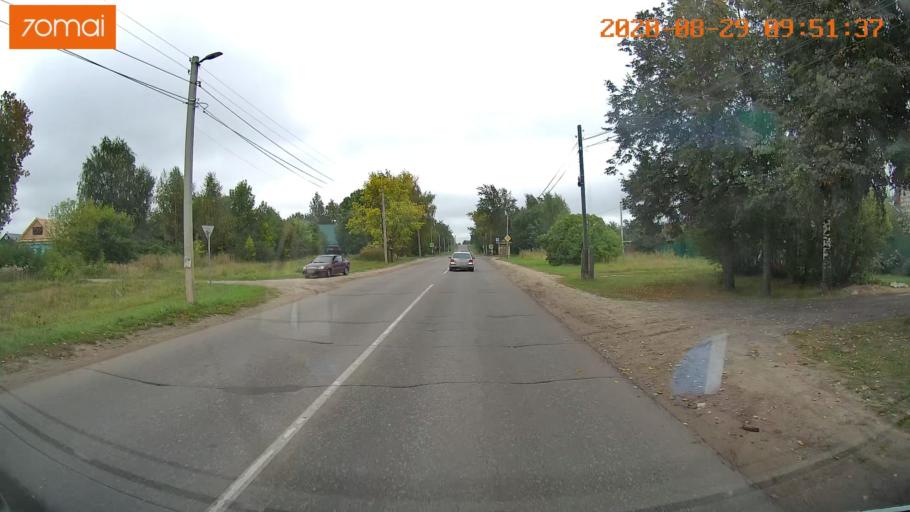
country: RU
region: Ivanovo
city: Kineshma
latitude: 57.4287
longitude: 42.2002
